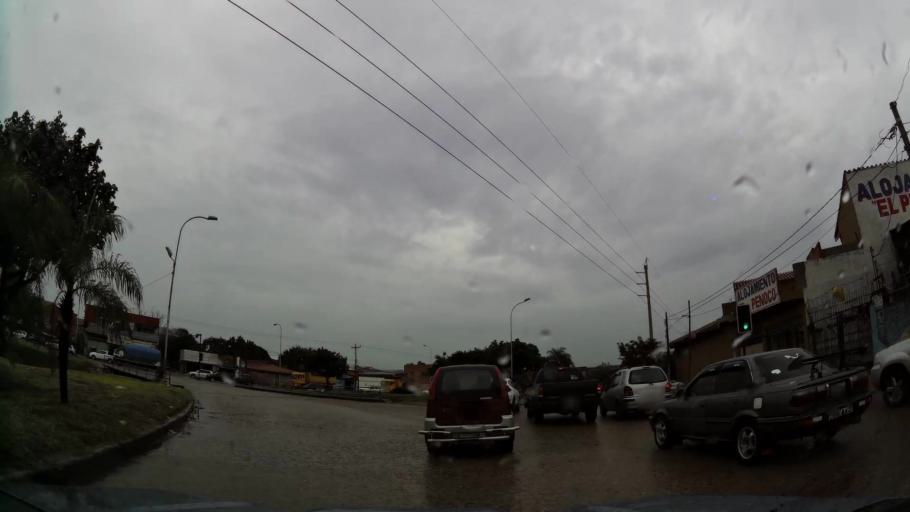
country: BO
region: Santa Cruz
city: Santa Cruz de la Sierra
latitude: -17.7970
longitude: -63.2159
